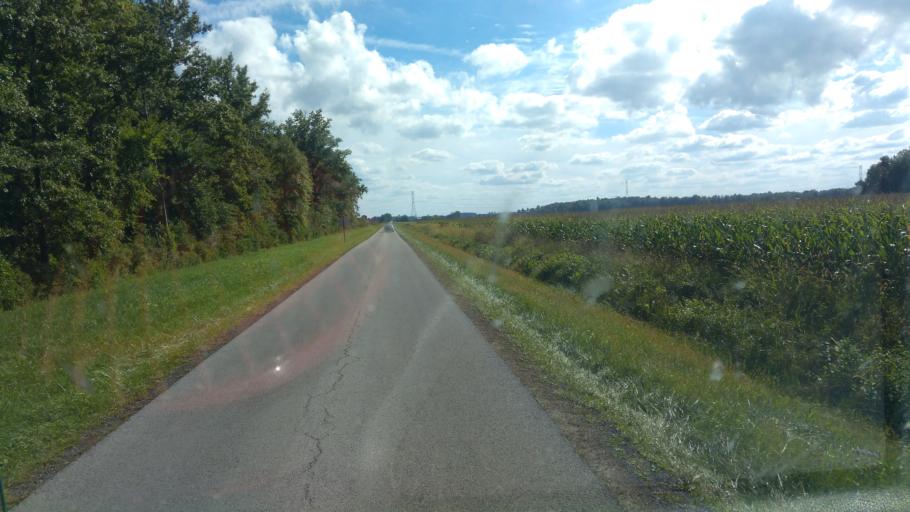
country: US
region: Ohio
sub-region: Sandusky County
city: Clyde
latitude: 41.4078
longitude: -82.9633
